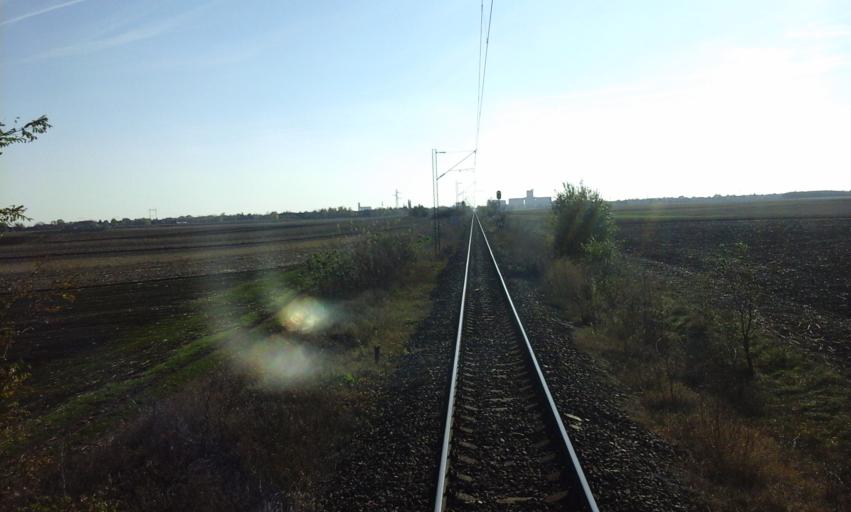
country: RS
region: Autonomna Pokrajina Vojvodina
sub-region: Severnobacki Okrug
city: Backa Topola
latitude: 45.8379
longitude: 19.6526
